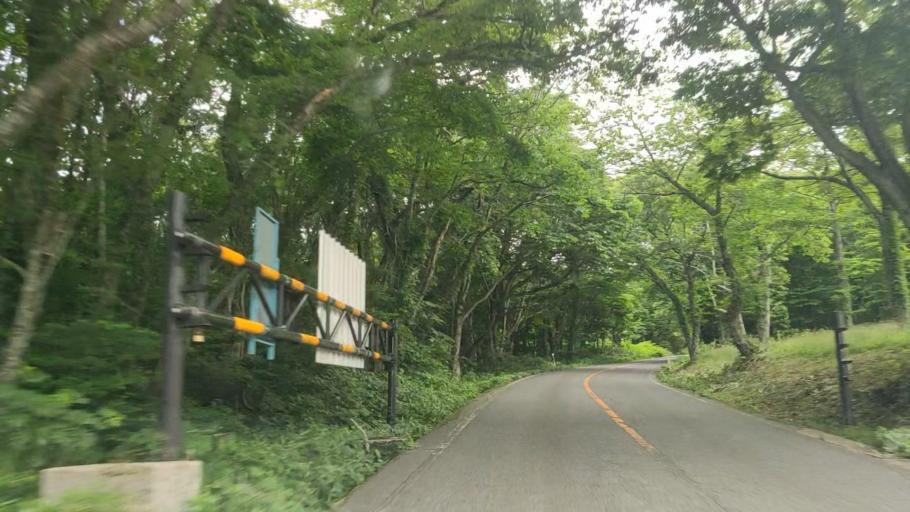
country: JP
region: Tottori
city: Yonago
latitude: 35.3404
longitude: 133.5556
